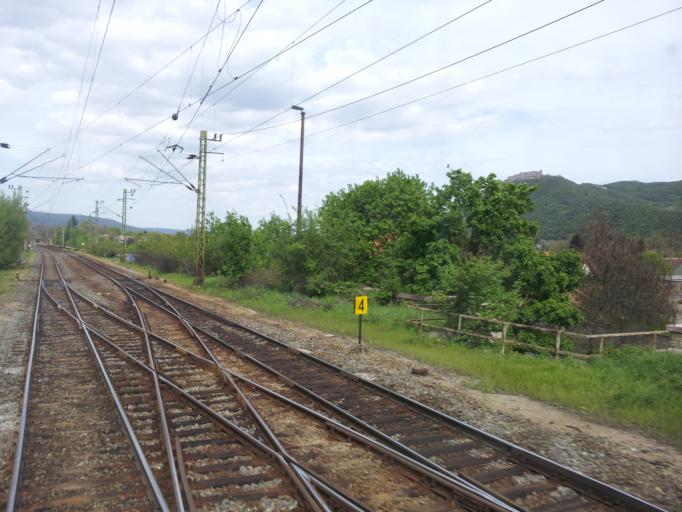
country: HU
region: Pest
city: Nagymaros
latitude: 47.7866
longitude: 18.9566
